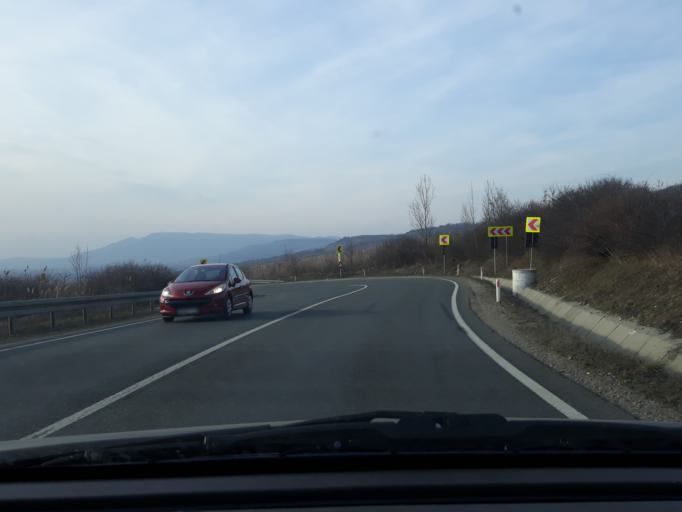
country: RO
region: Salaj
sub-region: Comuna Varsolt
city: Varsolt
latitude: 47.2155
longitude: 22.9288
